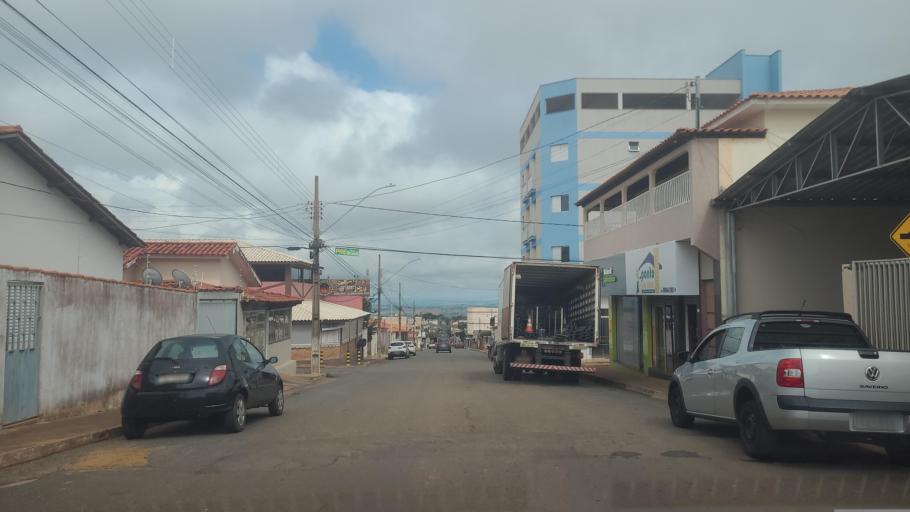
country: BR
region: Minas Gerais
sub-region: Carmo Do Paranaiba
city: Carmo do Paranaiba
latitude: -19.1957
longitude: -46.2399
